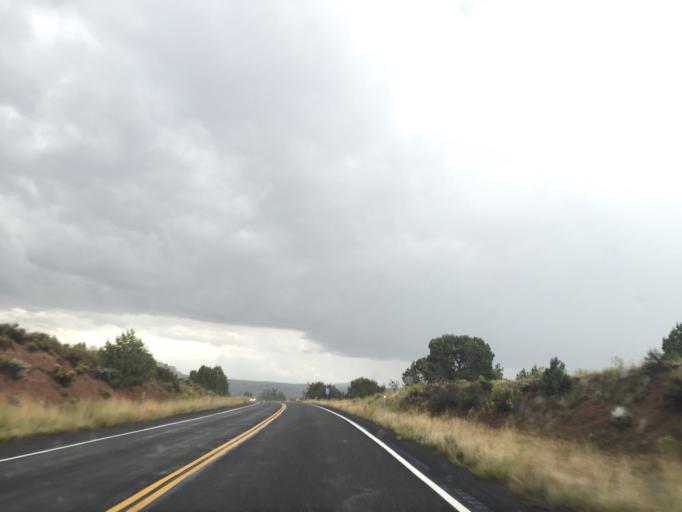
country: US
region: Utah
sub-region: Kane County
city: Kanab
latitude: 37.2277
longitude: -112.7272
